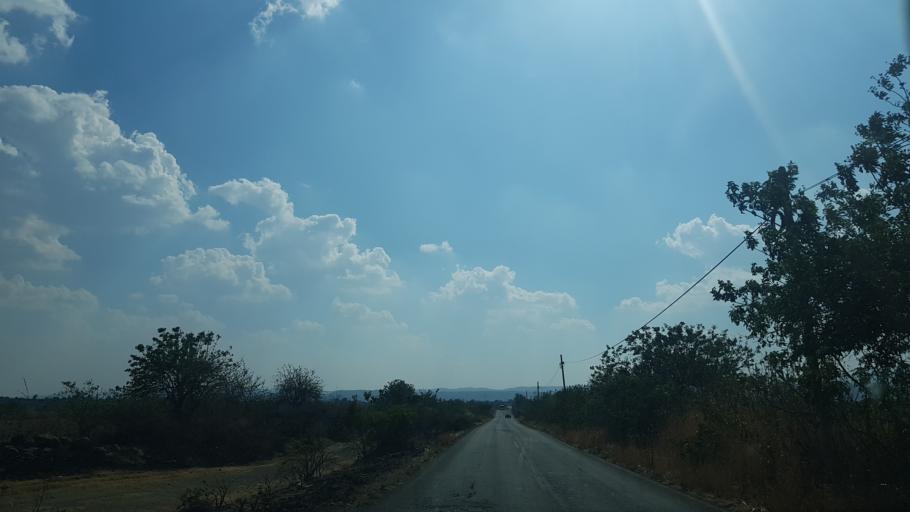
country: MX
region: Puebla
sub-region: Atlixco
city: Colonia Agricola de Ocotepec (Colonia San Jose)
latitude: 18.8978
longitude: -98.5019
